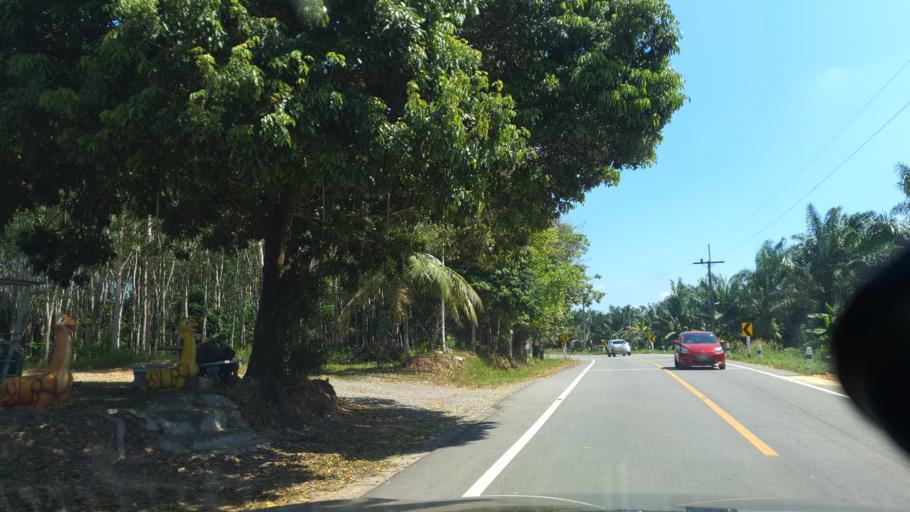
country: TH
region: Krabi
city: Khlong Thom
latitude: 7.9301
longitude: 99.2265
